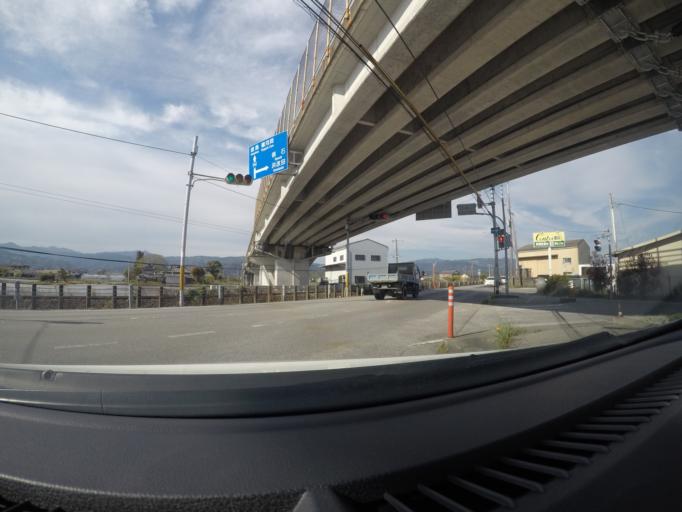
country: JP
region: Kochi
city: Kochi-shi
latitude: 33.5946
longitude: 133.6659
